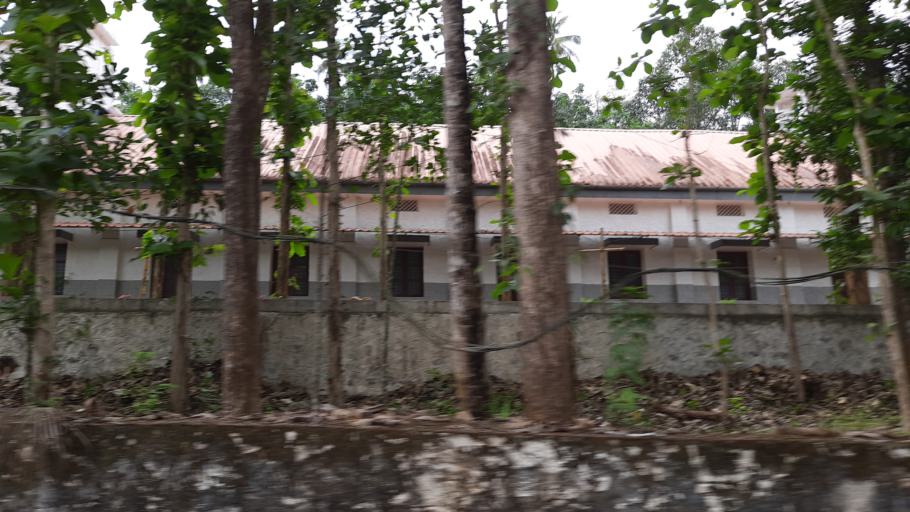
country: IN
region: Kerala
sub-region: Kottayam
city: Lalam
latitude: 9.8208
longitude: 76.7504
